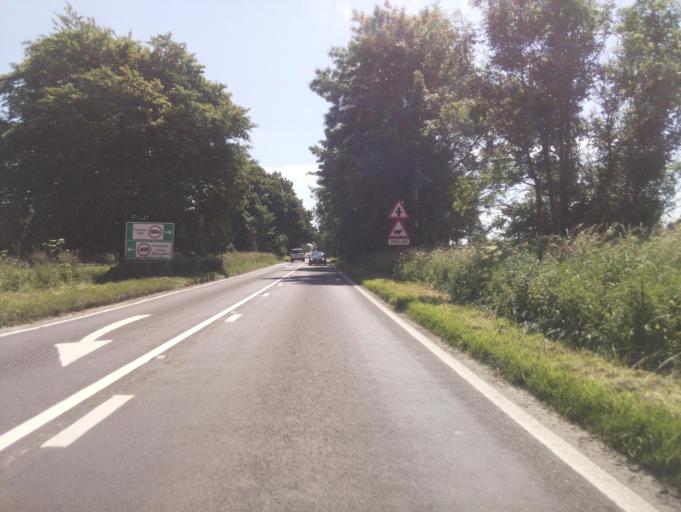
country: GB
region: England
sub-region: Derbyshire
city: Buxton
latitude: 53.2368
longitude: -1.8899
